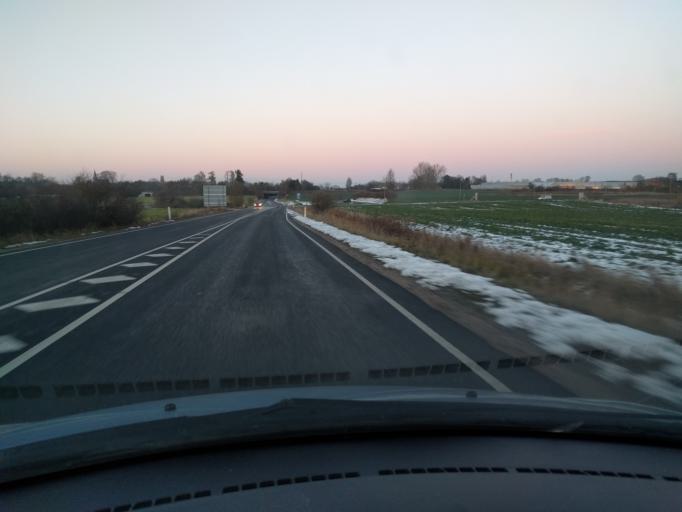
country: DK
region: South Denmark
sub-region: Nyborg Kommune
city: Nyborg
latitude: 55.3329
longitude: 10.7414
